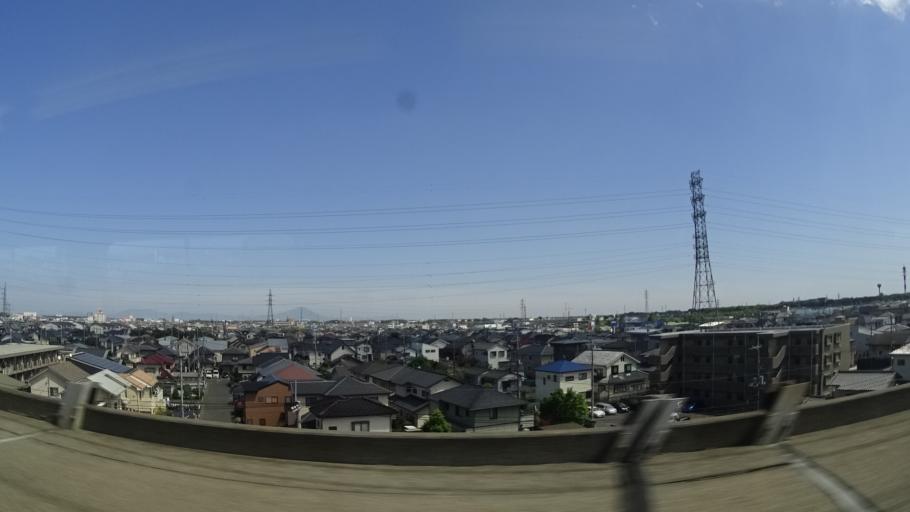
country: JP
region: Tochigi
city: Oyama
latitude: 36.2988
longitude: 139.7963
